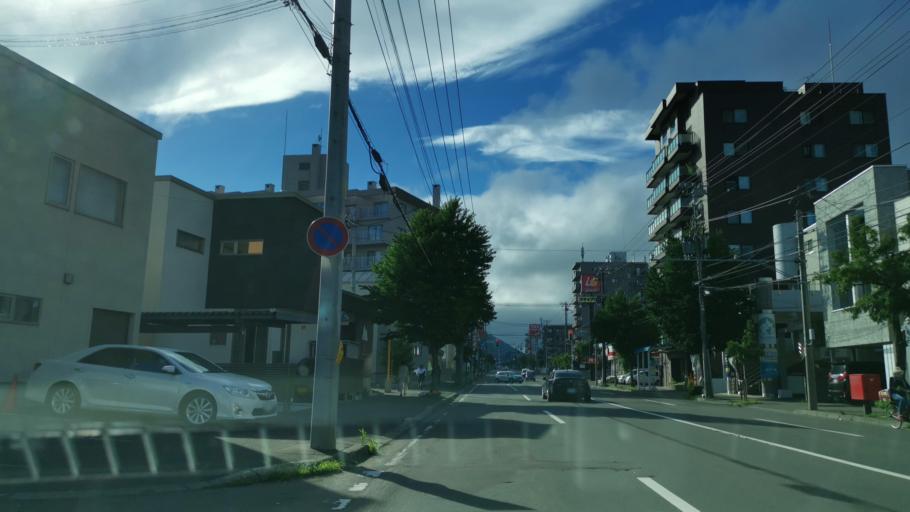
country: JP
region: Hokkaido
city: Sapporo
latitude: 43.0640
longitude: 141.3018
